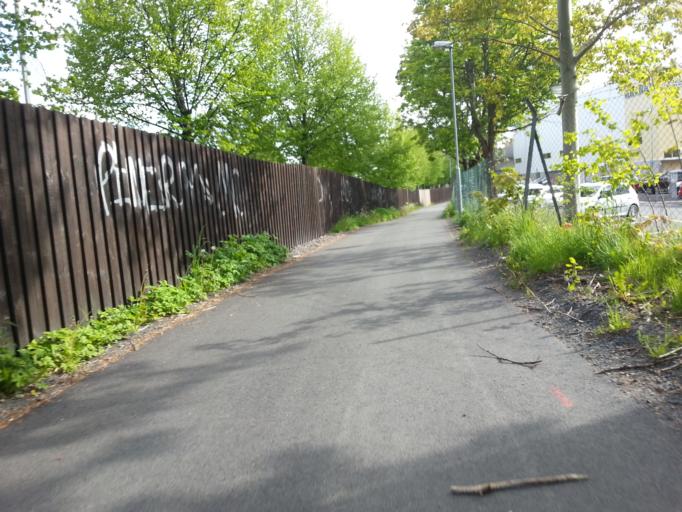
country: SE
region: Joenkoeping
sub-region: Jonkopings Kommun
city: Jonkoping
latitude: 57.7809
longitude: 14.1509
